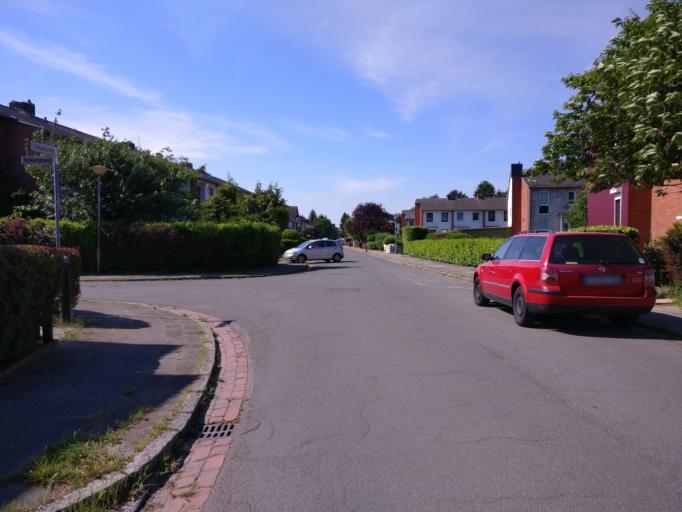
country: DE
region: Lower Saxony
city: Lilienthal
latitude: 53.1053
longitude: 8.8693
